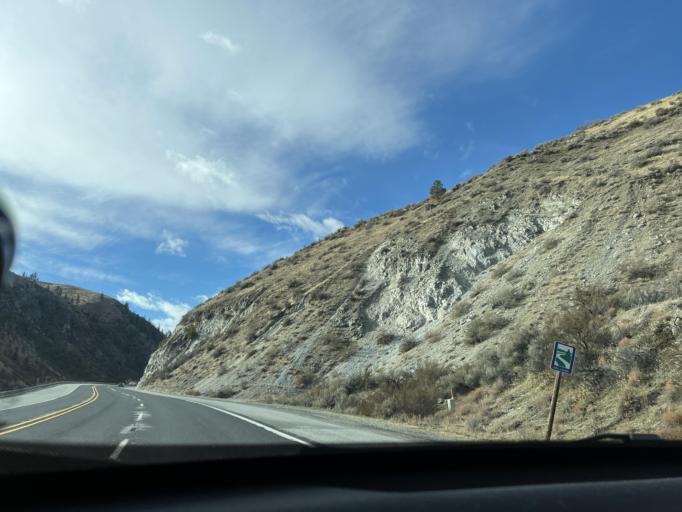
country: US
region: Washington
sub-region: Chelan County
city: Manson
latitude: 47.8334
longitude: -120.1120
